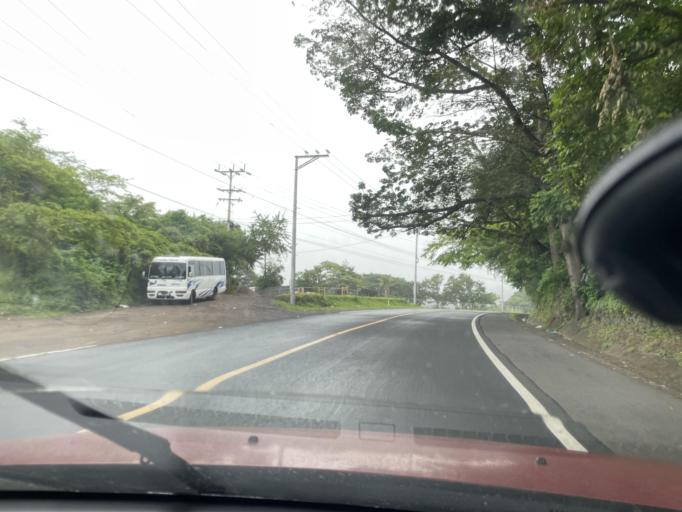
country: SV
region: San Miguel
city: San Miguel
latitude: 13.5307
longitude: -88.1402
